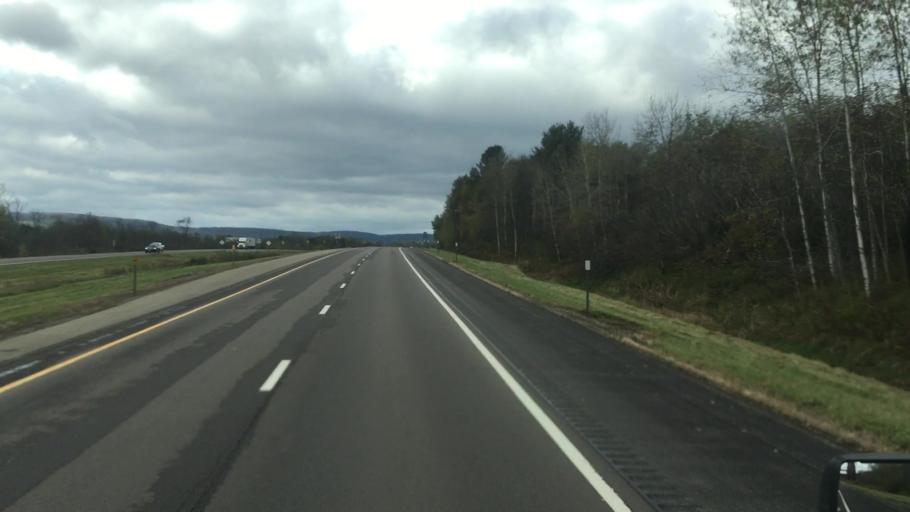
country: US
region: New York
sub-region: Allegany County
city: Belmont
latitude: 42.2550
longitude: -78.0679
